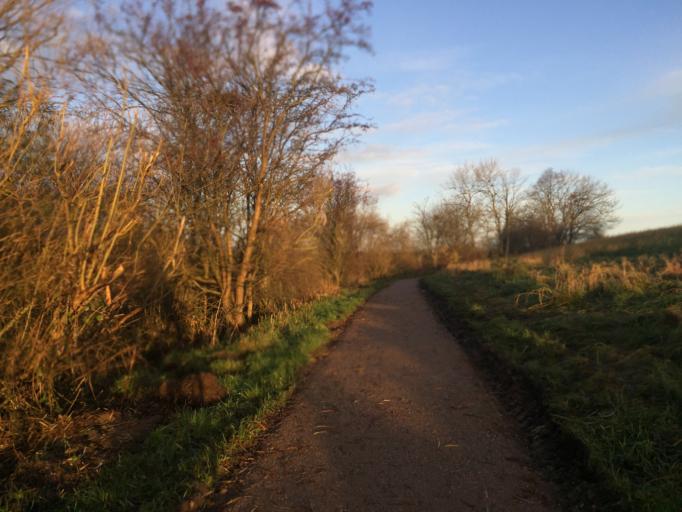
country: DK
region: Zealand
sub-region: Ringsted Kommune
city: Ringsted
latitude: 55.4220
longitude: 11.7761
